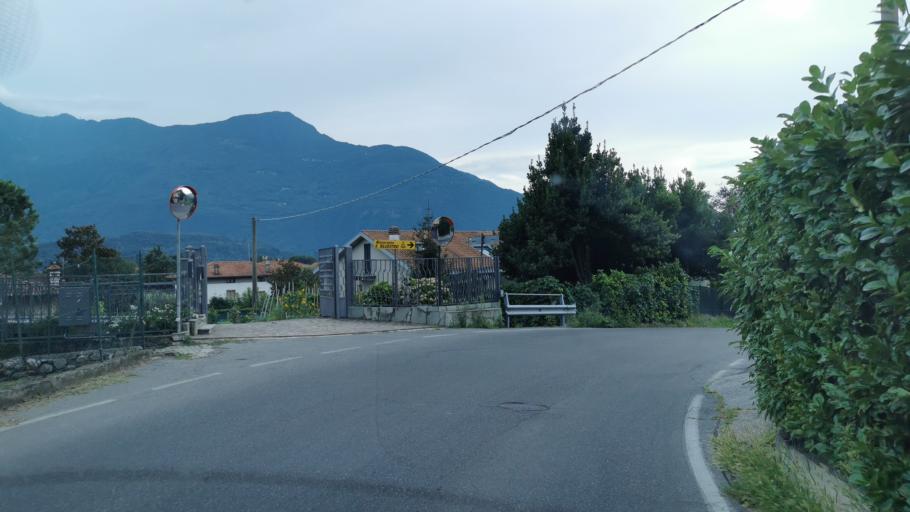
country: IT
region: Lombardy
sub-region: Provincia di Como
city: Domaso
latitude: 46.1554
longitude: 9.3336
